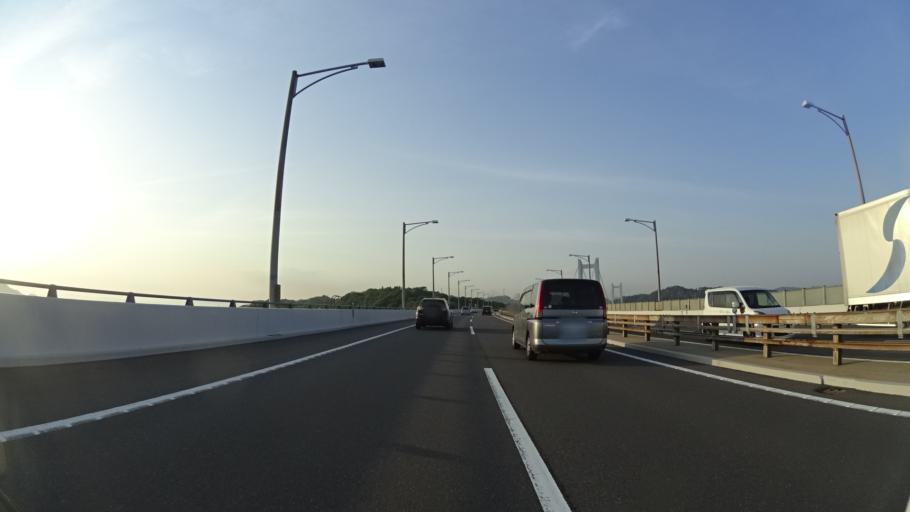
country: JP
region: Kagawa
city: Sakaidecho
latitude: 34.4187
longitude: 133.8042
